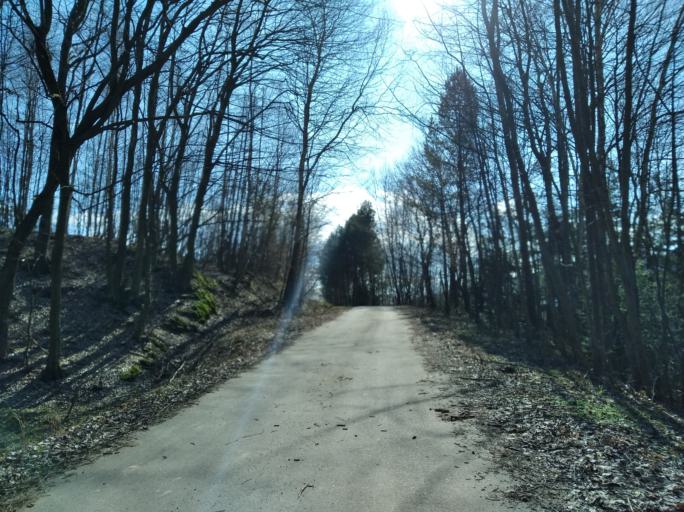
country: PL
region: Subcarpathian Voivodeship
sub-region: Powiat strzyzowski
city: Wysoka Strzyzowska
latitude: 49.8083
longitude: 21.7510
